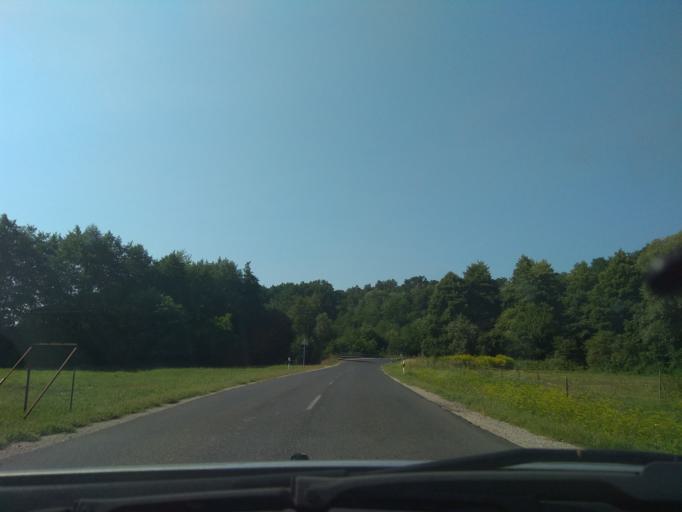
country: HU
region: Borsod-Abauj-Zemplen
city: Harsany
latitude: 47.9978
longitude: 20.7584
